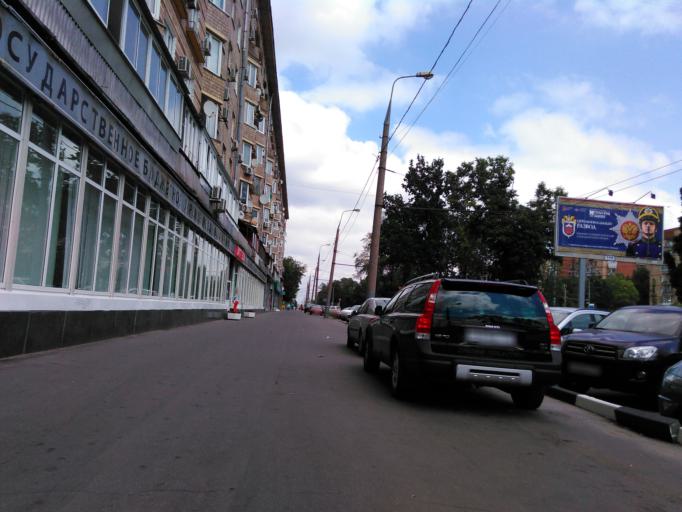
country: RU
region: Moskovskaya
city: Semenovskoye
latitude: 55.6765
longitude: 37.5273
